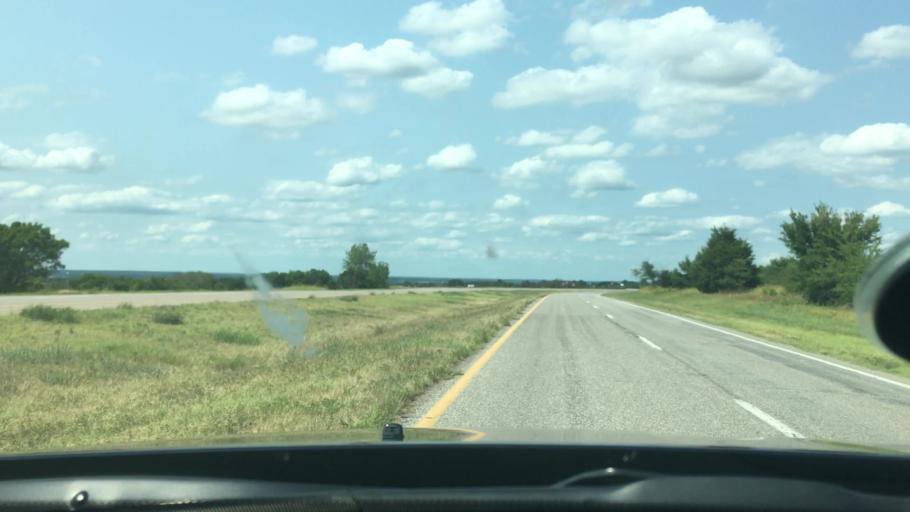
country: US
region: Oklahoma
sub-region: Pontotoc County
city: Ada
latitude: 34.7059
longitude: -96.7311
